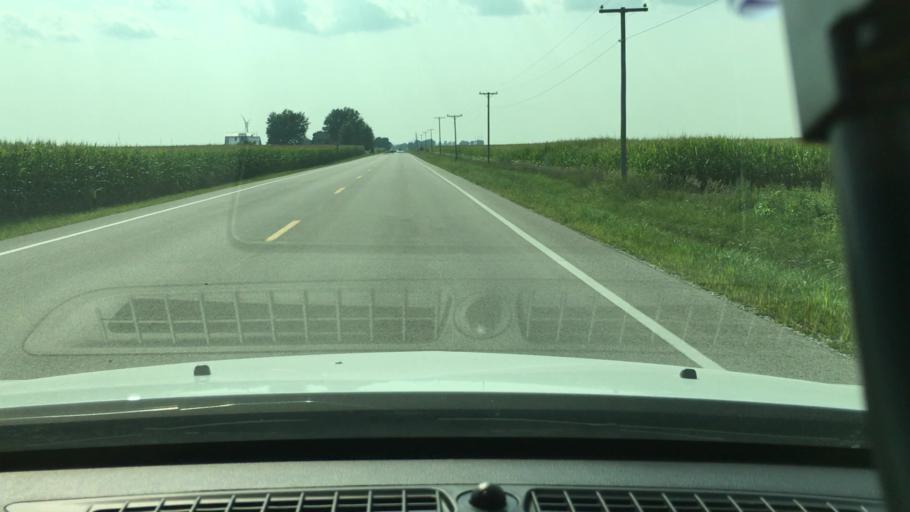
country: US
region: Illinois
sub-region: DeKalb County
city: Malta
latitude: 41.8487
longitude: -88.8490
